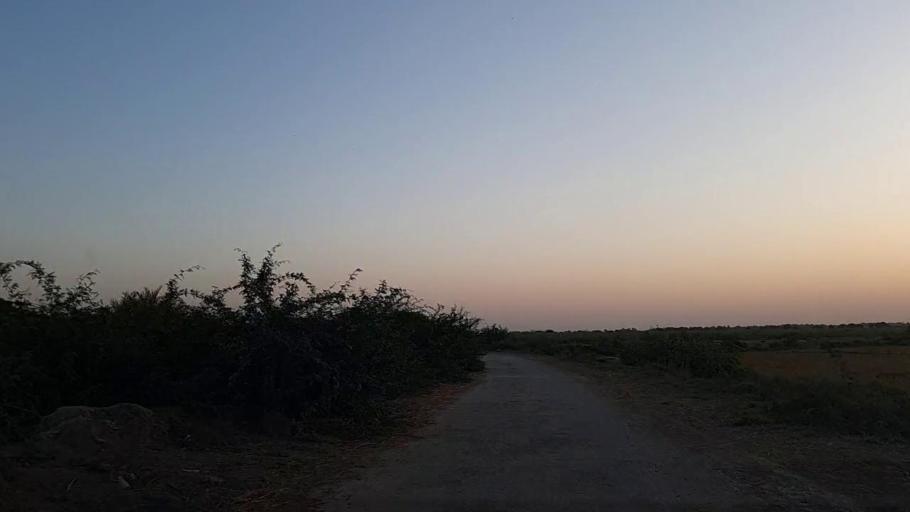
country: PK
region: Sindh
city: Mirpur Batoro
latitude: 24.6283
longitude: 68.1841
